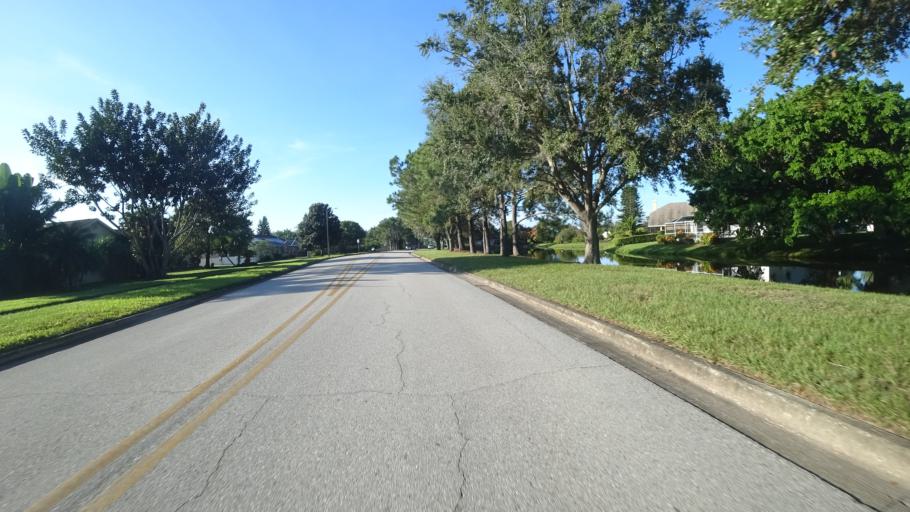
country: US
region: Florida
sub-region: Manatee County
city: Ellenton
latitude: 27.4894
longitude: -82.5028
